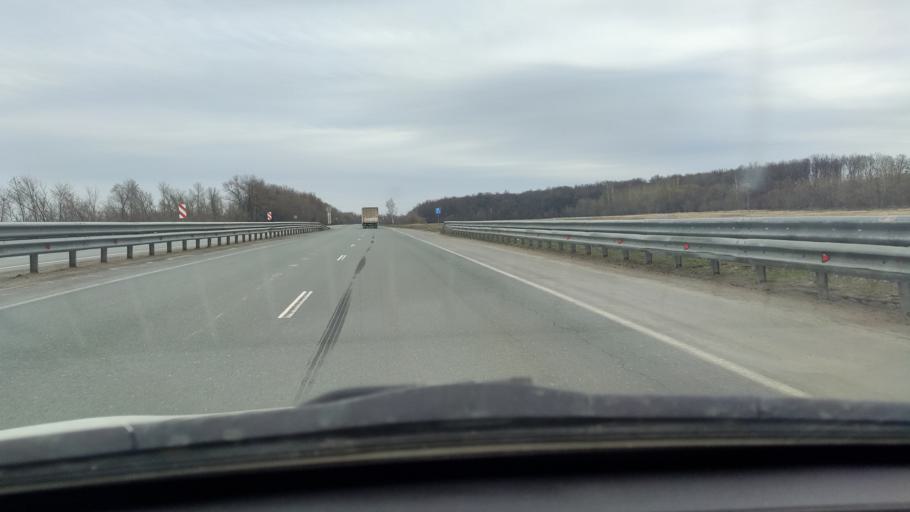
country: RU
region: Samara
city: Zhigulevsk
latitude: 53.2838
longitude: 49.3234
